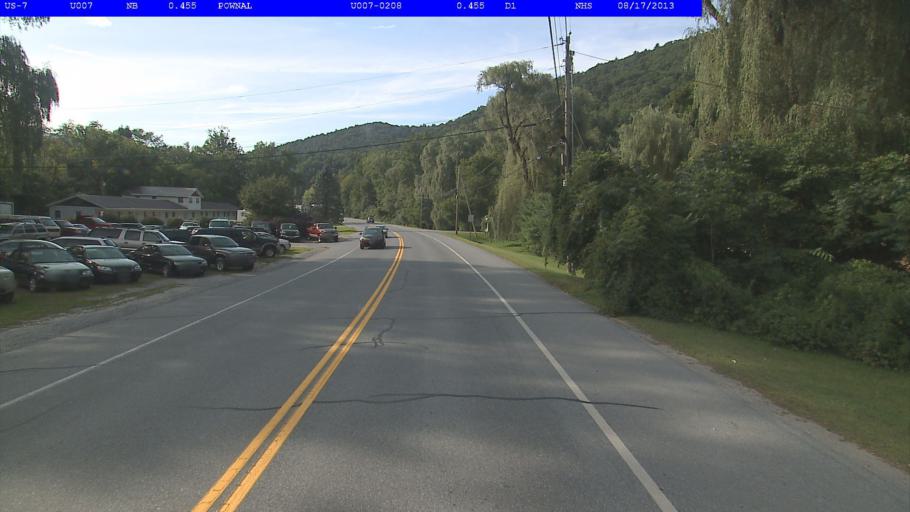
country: US
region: Massachusetts
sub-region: Berkshire County
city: Williamstown
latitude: 42.7513
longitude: -73.2153
